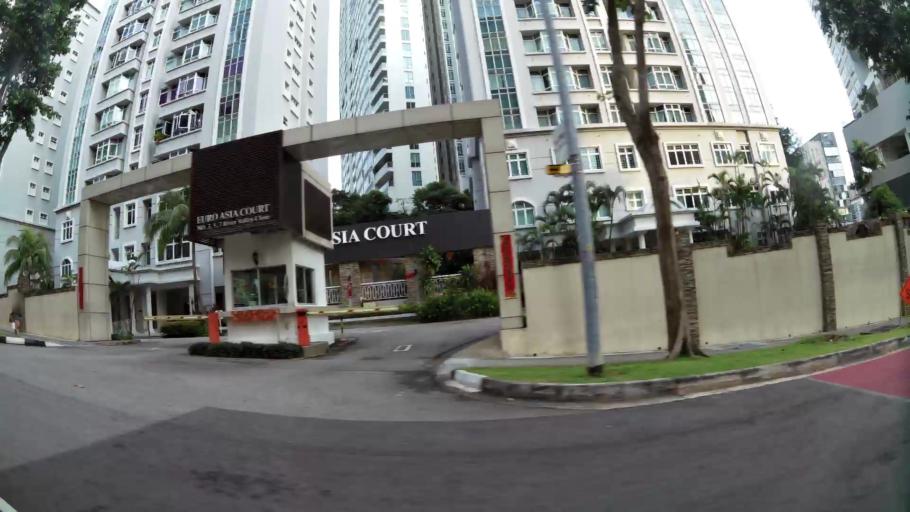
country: SG
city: Singapore
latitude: 1.2943
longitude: 103.8373
